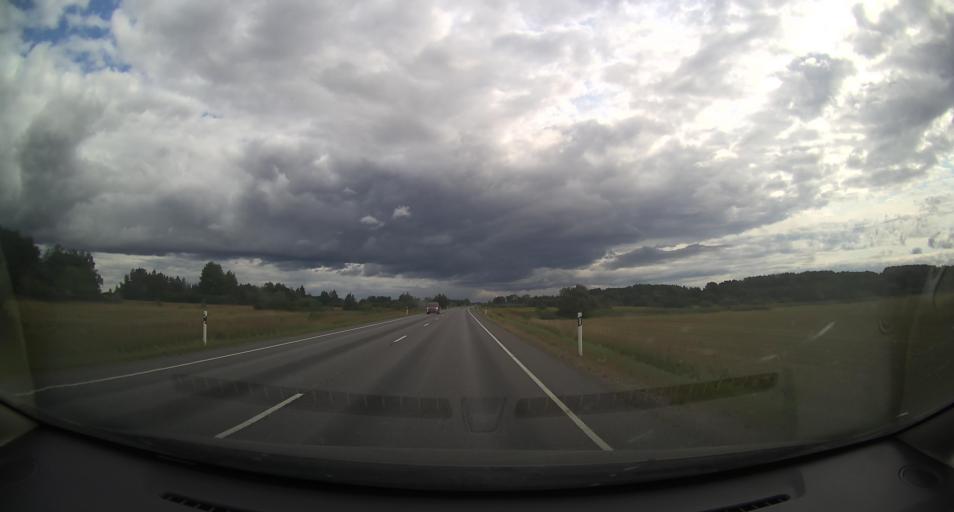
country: EE
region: Laeaene
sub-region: Lihula vald
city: Lihula
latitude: 58.7176
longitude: 23.8819
